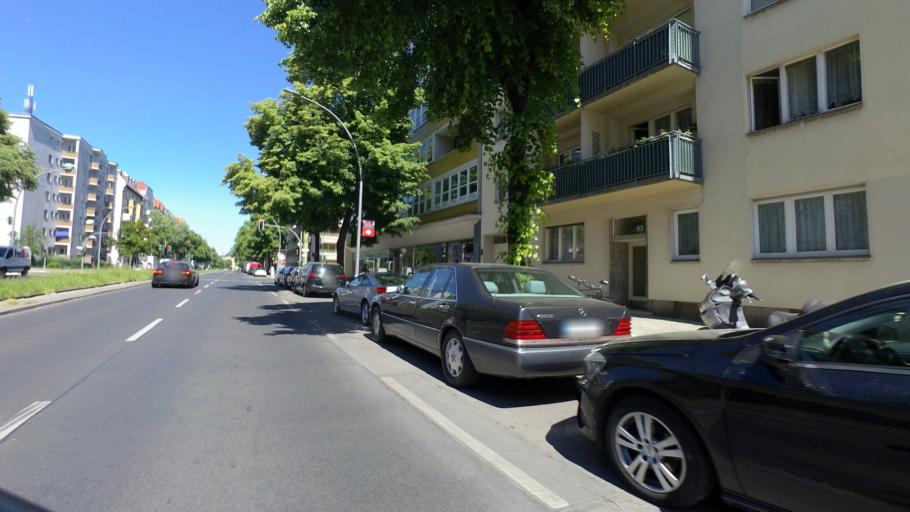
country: DE
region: Berlin
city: Charlottenburg Bezirk
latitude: 52.5129
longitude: 13.3013
